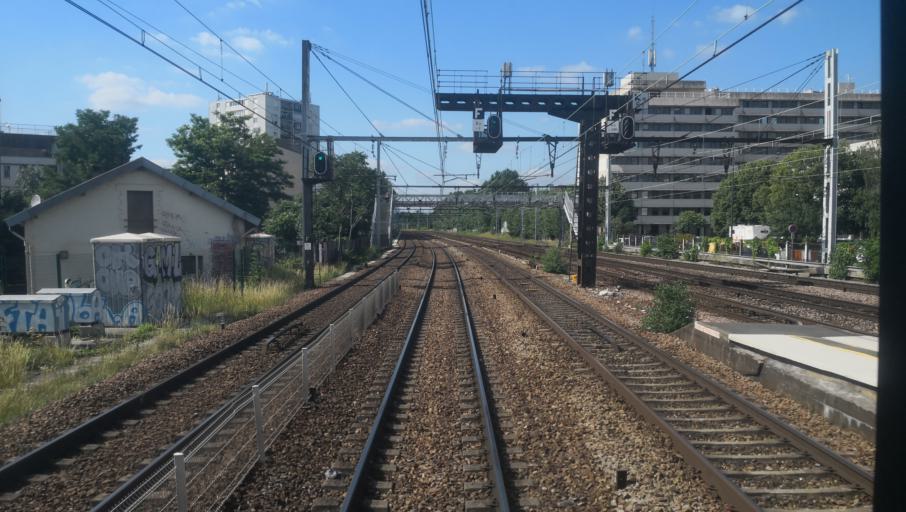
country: FR
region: Ile-de-France
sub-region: Departement du Val-de-Marne
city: Alfortville
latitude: 48.8035
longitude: 2.4259
